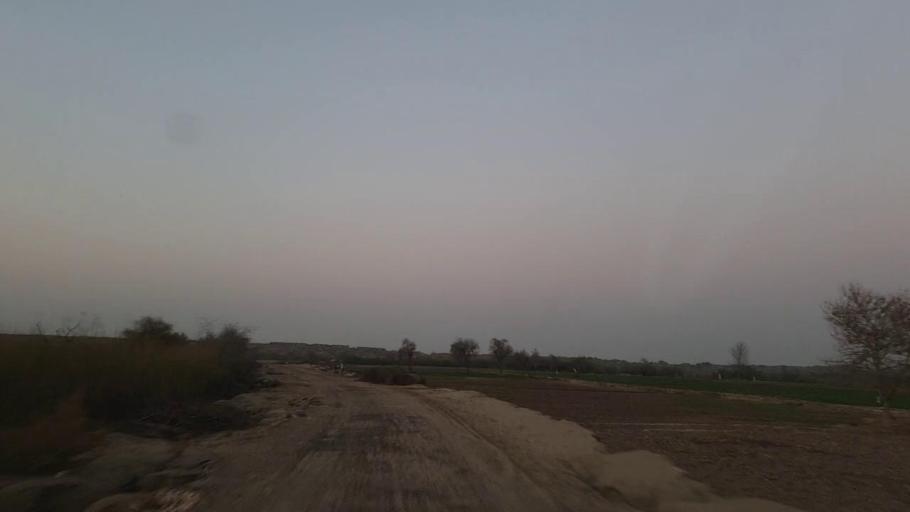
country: PK
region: Sindh
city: Bandhi
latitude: 26.6185
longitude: 68.3938
